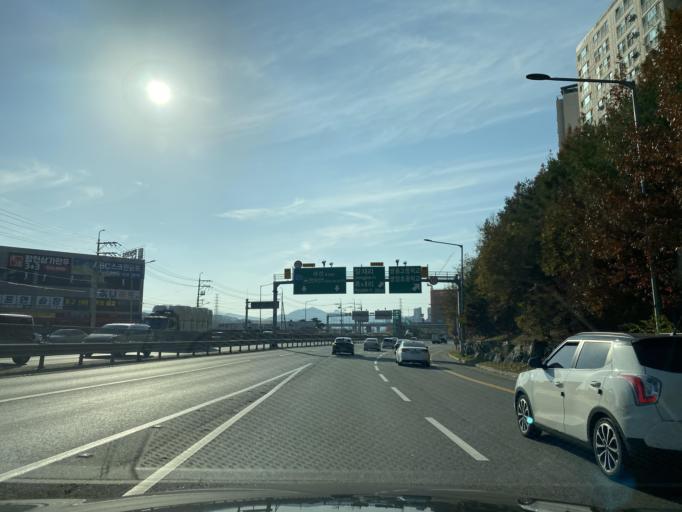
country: KR
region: Chungcheongnam-do
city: Cheonan
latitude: 36.7854
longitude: 127.1157
